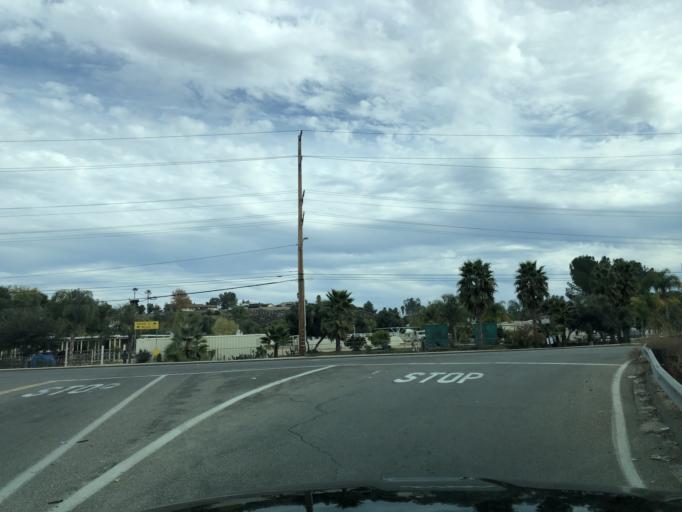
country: US
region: California
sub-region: Riverside County
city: Wildomar
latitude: 33.6147
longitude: -117.2901
